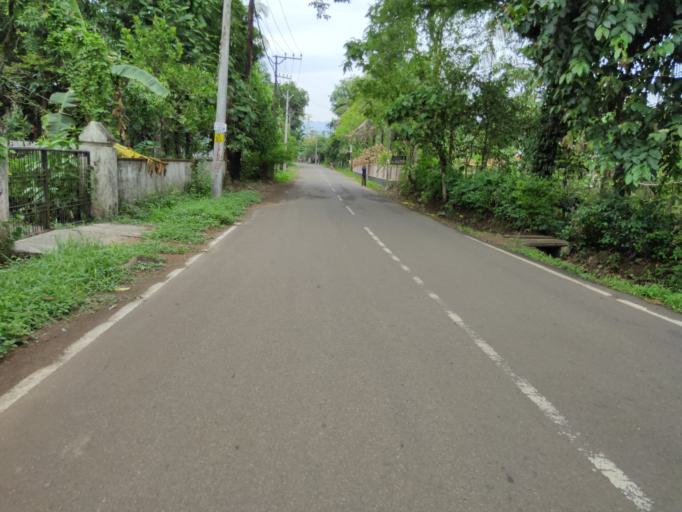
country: IN
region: Kerala
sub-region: Malappuram
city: Manjeri
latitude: 11.2650
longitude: 76.2355
